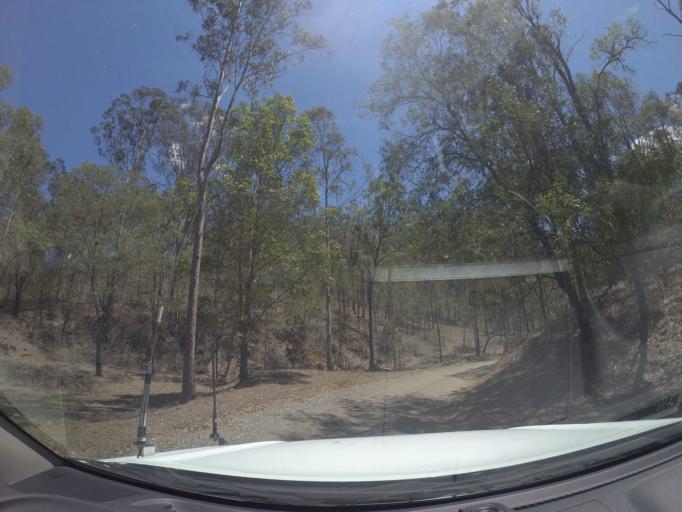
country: AU
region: Queensland
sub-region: Ipswich
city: Deebing Heights
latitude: -27.7636
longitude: 152.8080
